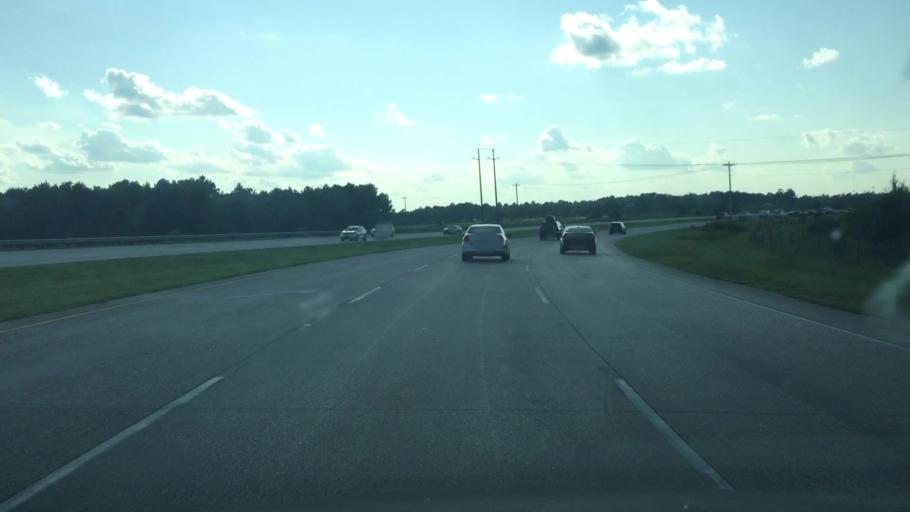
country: US
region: South Carolina
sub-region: Horry County
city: North Myrtle Beach
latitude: 33.8382
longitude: -78.6956
